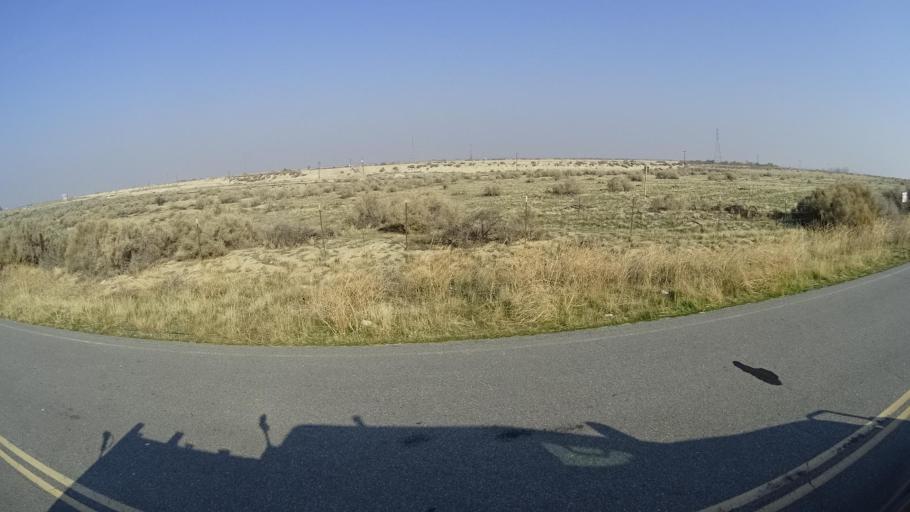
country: US
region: California
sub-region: Kern County
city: Buttonwillow
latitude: 35.2886
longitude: -119.3414
